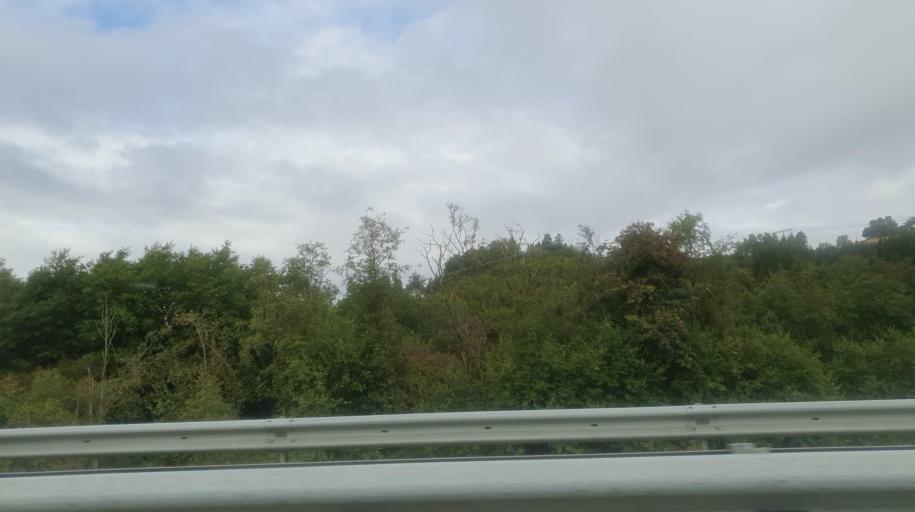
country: NO
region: Nord-Trondelag
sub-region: Levanger
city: Levanger
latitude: 63.7325
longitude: 11.3109
